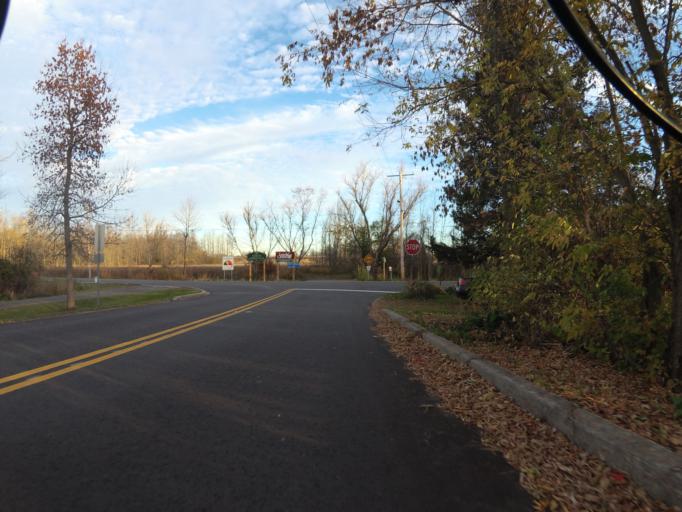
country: CA
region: Ontario
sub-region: Lanark County
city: Smiths Falls
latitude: 44.9679
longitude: -75.8088
